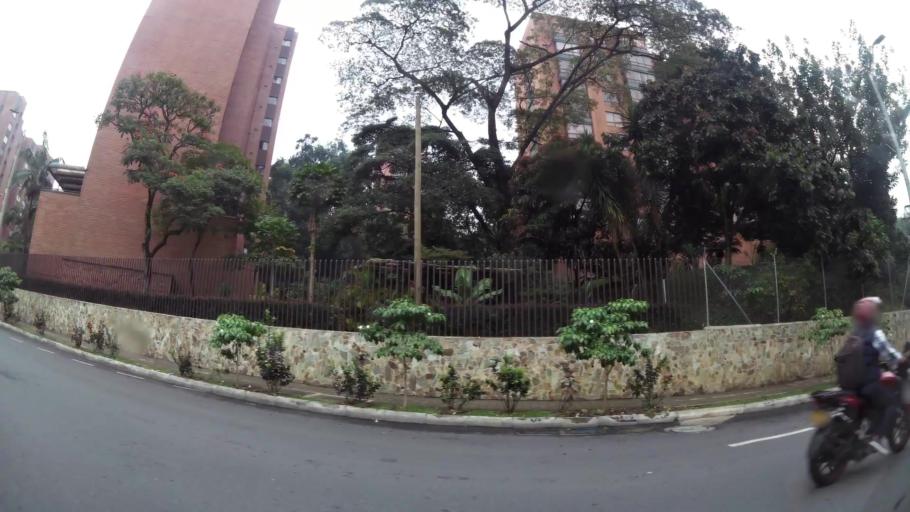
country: CO
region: Antioquia
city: Envigado
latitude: 6.1905
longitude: -75.5679
